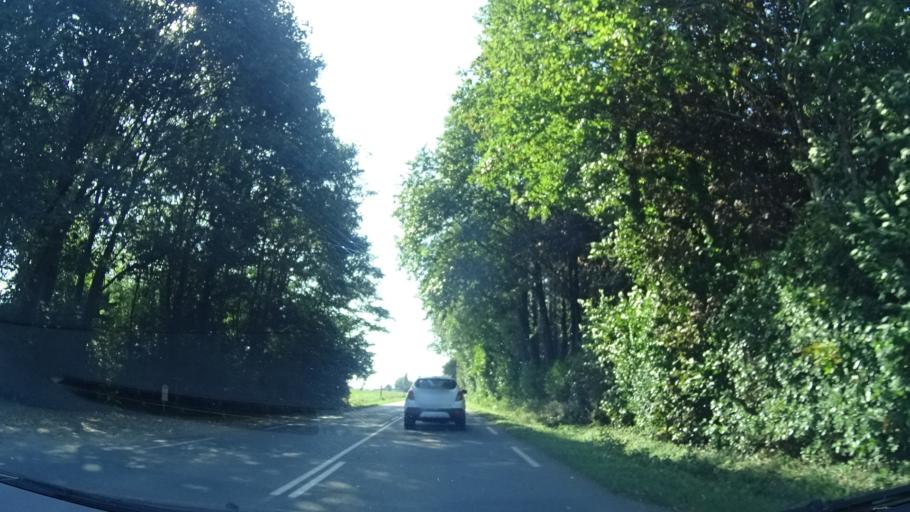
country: FR
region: Brittany
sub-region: Departement du Finistere
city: Plonevez-Porzay
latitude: 48.0963
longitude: -4.2559
